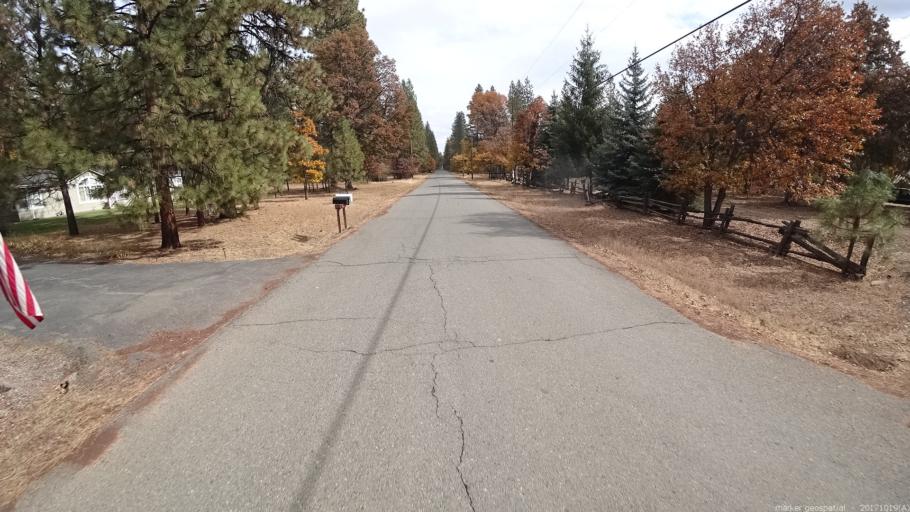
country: US
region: California
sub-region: Shasta County
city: Burney
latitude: 41.0800
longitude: -121.5255
